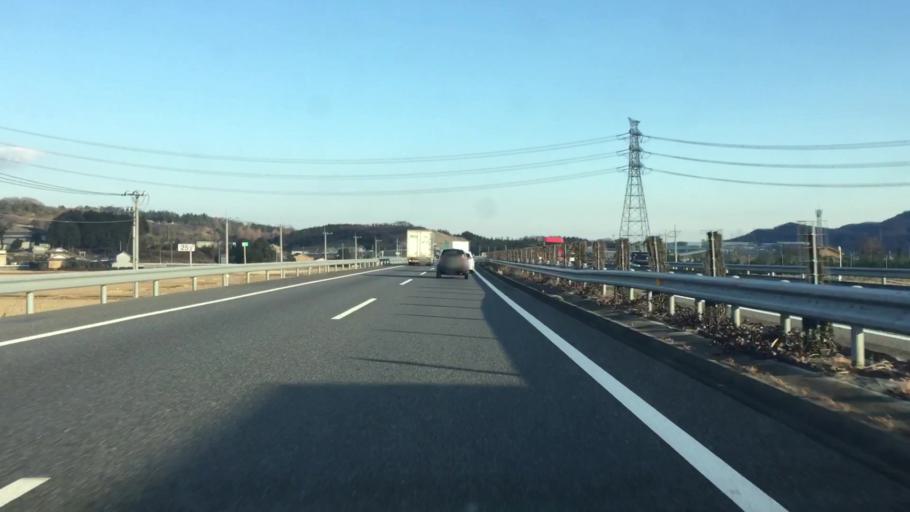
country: JP
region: Gunma
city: Ota
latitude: 36.3435
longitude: 139.3373
